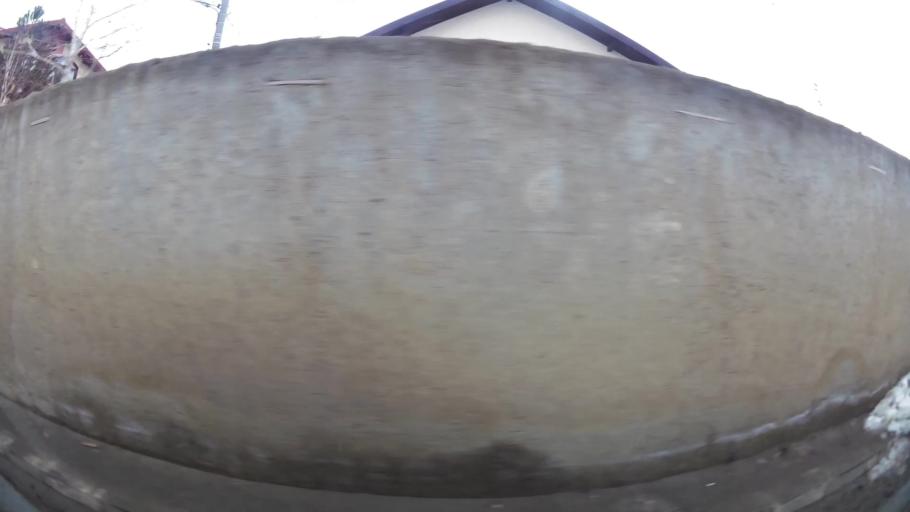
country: RO
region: Ilfov
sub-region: Comuna Pantelimon
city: Pantelimon
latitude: 44.4608
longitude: 26.2182
